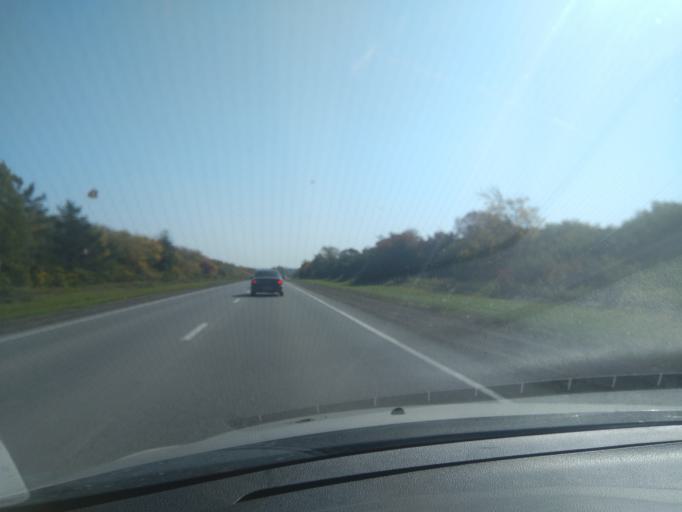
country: RU
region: Sverdlovsk
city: Sovkhoznyy
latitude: 56.5740
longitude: 61.3338
